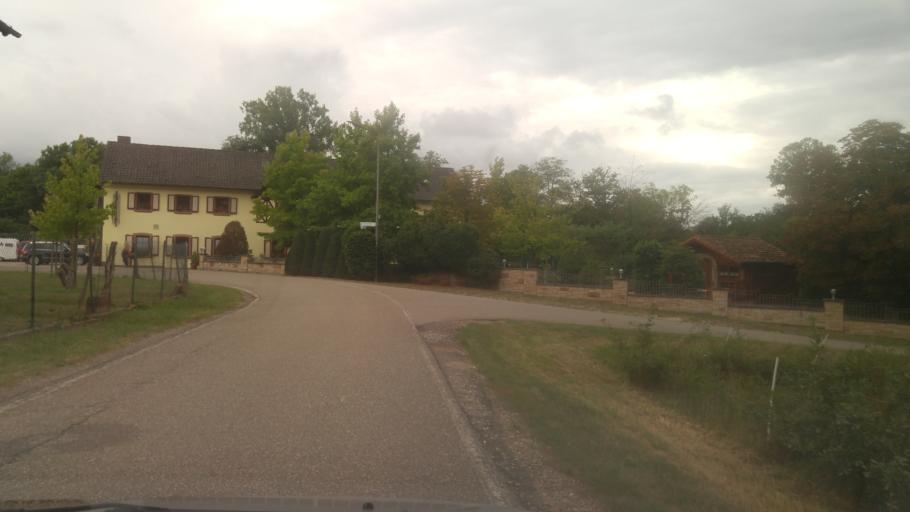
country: DE
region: Rheinland-Pfalz
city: Steinfeld
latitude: 48.9992
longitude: 8.0708
